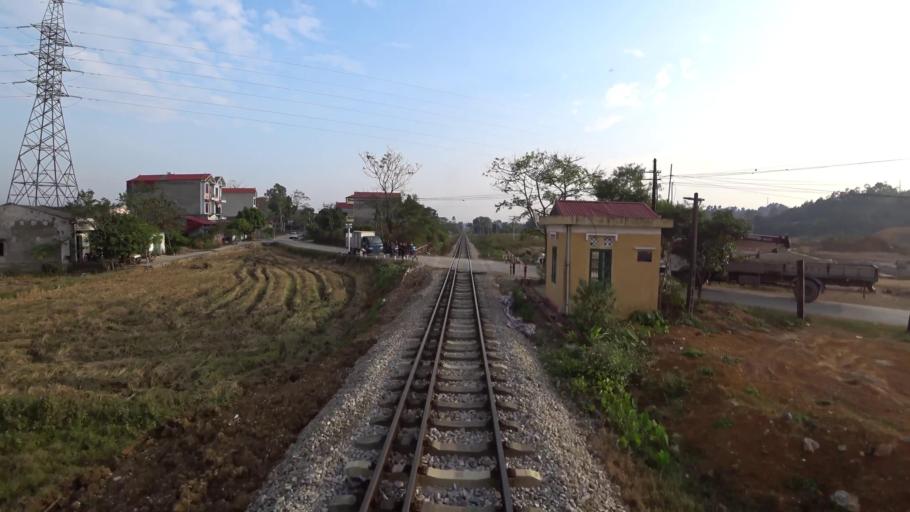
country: VN
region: Lang Son
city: Thi Tran Cao Loc
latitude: 21.8854
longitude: 106.7463
